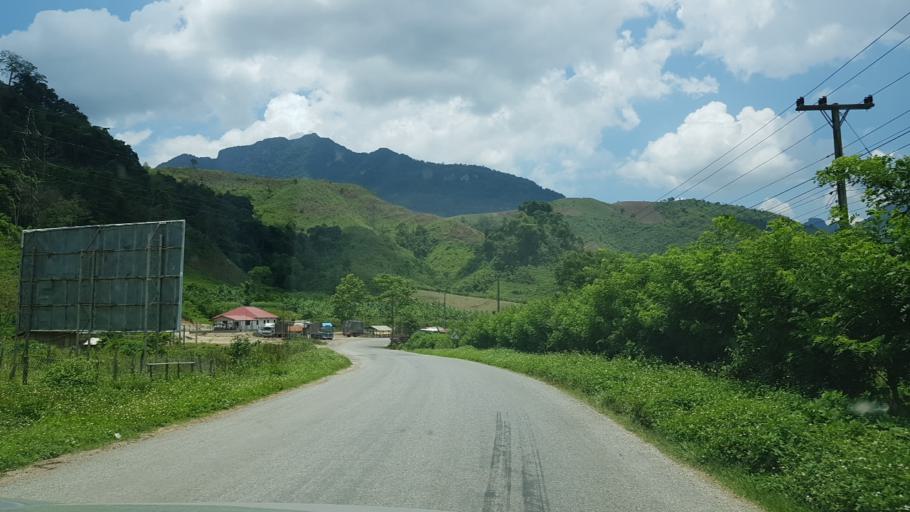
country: LA
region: Vientiane
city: Muang Kasi
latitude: 19.1406
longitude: 102.3108
